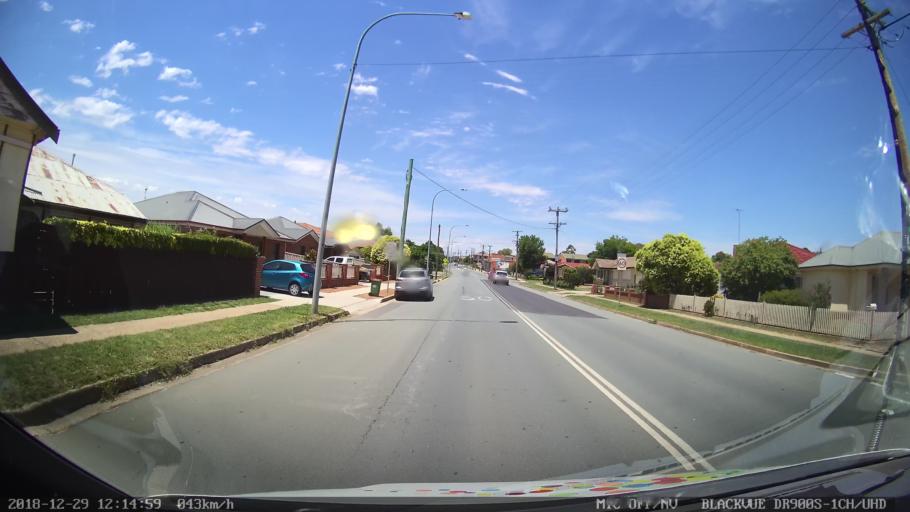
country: AU
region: New South Wales
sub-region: Queanbeyan
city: Queanbeyan
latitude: -35.3586
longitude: 149.2332
